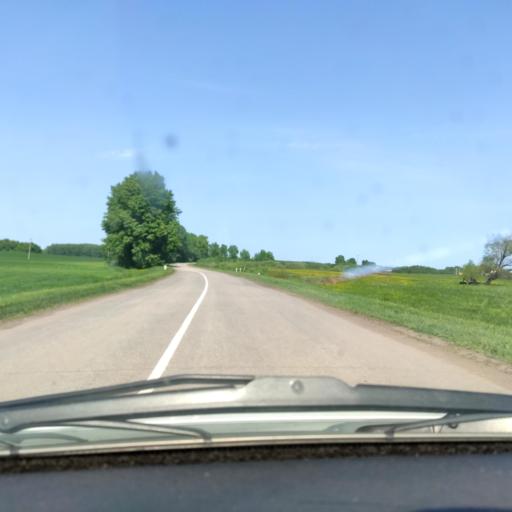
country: RU
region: Bashkortostan
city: Chishmy
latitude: 54.4810
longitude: 55.5702
